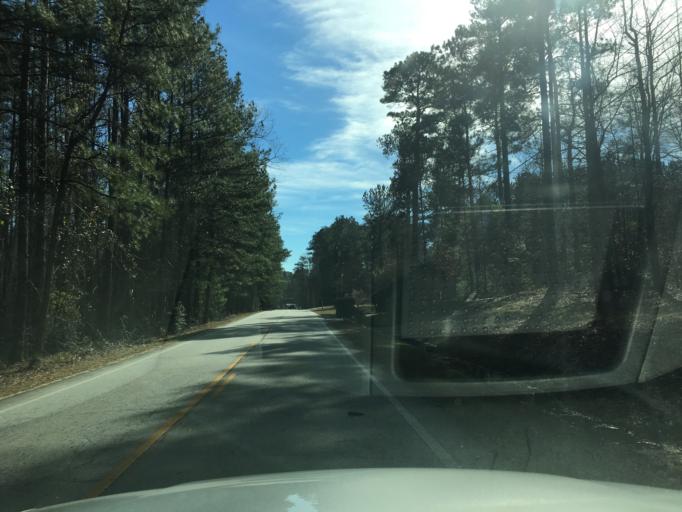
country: US
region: Georgia
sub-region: Rockdale County
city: Lakeview Estates
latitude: 33.7667
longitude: -84.0521
